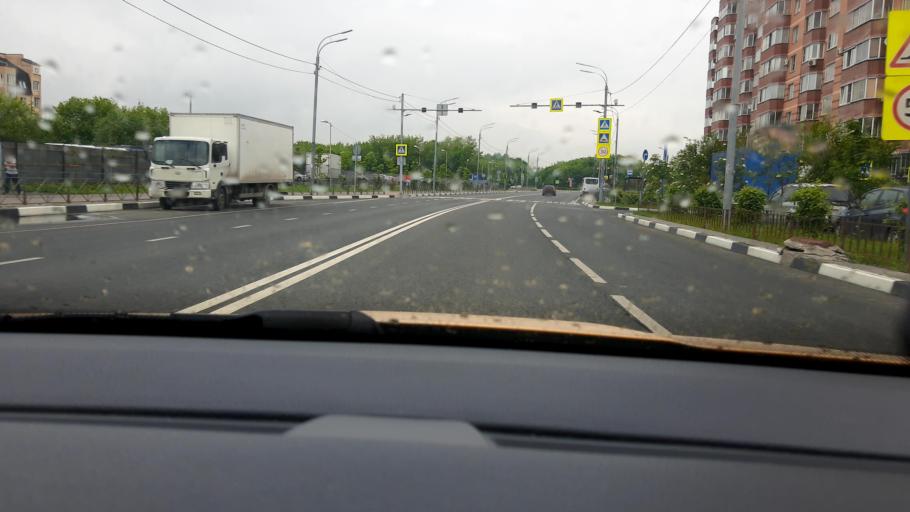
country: RU
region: Moscow
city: Vatutino
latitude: 55.9020
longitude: 37.7011
